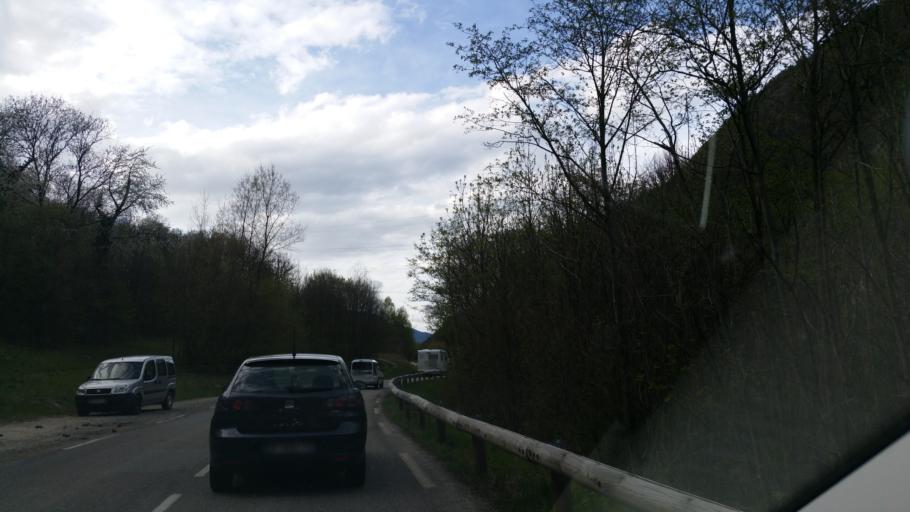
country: FR
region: Rhone-Alpes
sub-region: Departement de la Savoie
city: Saint-Jean-de-Maurienne
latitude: 45.3159
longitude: 6.3246
